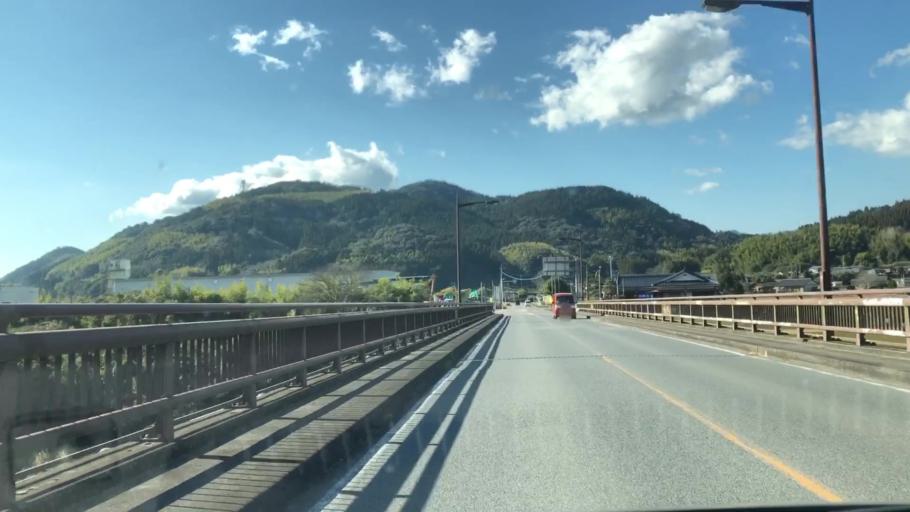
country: JP
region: Kagoshima
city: Satsumasendai
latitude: 31.8681
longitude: 130.4303
